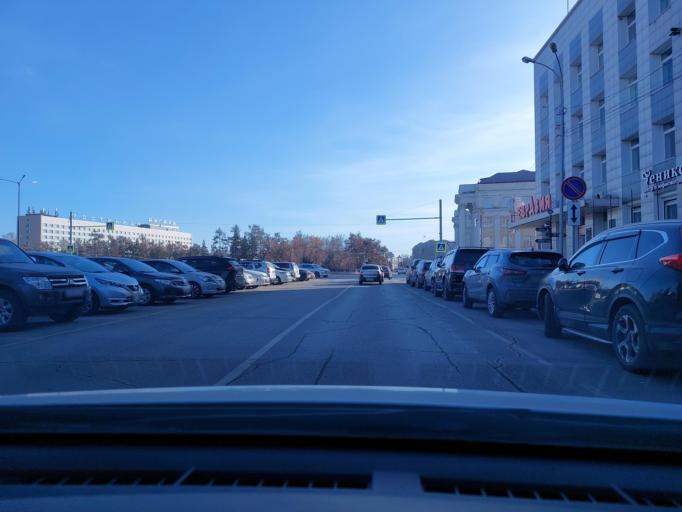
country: RU
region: Irkutsk
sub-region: Irkutskiy Rayon
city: Irkutsk
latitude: 52.2898
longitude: 104.2791
